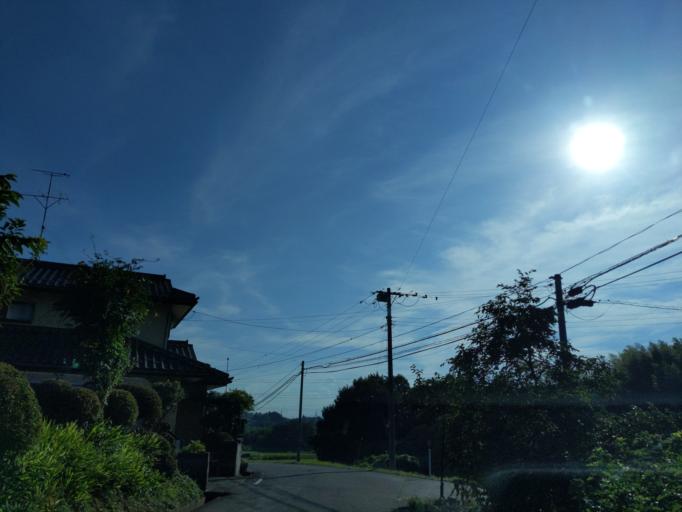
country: JP
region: Fukushima
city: Sukagawa
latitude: 37.3195
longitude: 140.4318
